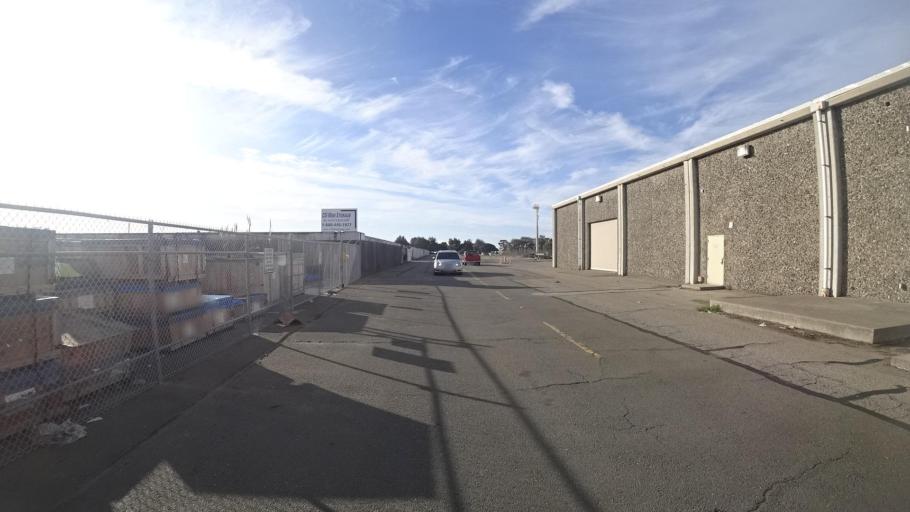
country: US
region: California
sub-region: Alameda County
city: Oakland
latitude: 37.7742
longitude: -122.2927
